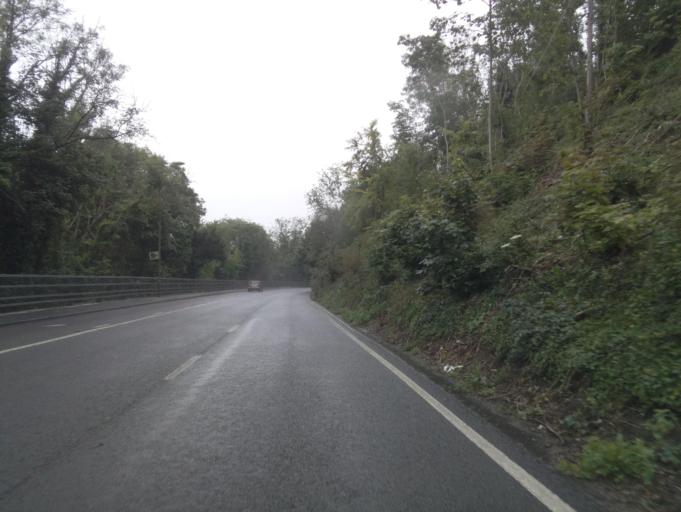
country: GB
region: England
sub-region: Surrey
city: Reigate
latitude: 51.2538
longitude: -0.1948
